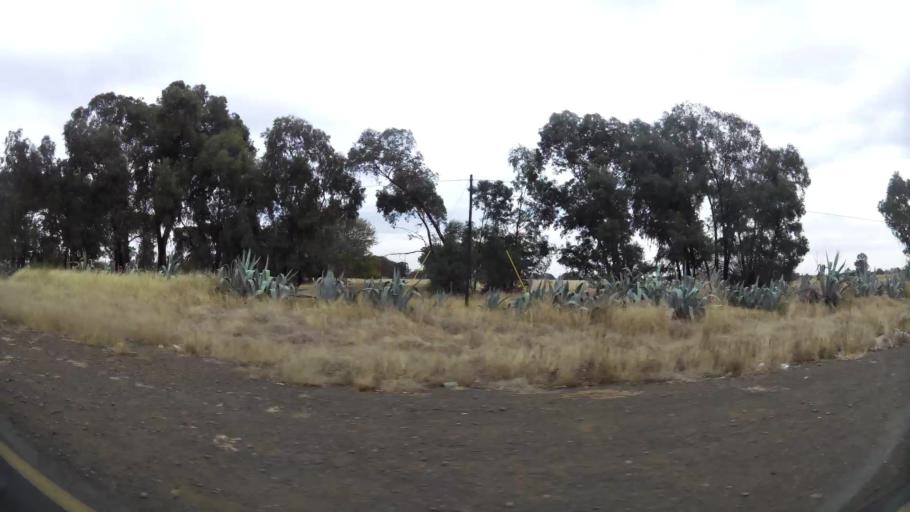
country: ZA
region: Orange Free State
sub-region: Fezile Dabi District Municipality
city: Kroonstad
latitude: -27.6196
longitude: 27.2336
